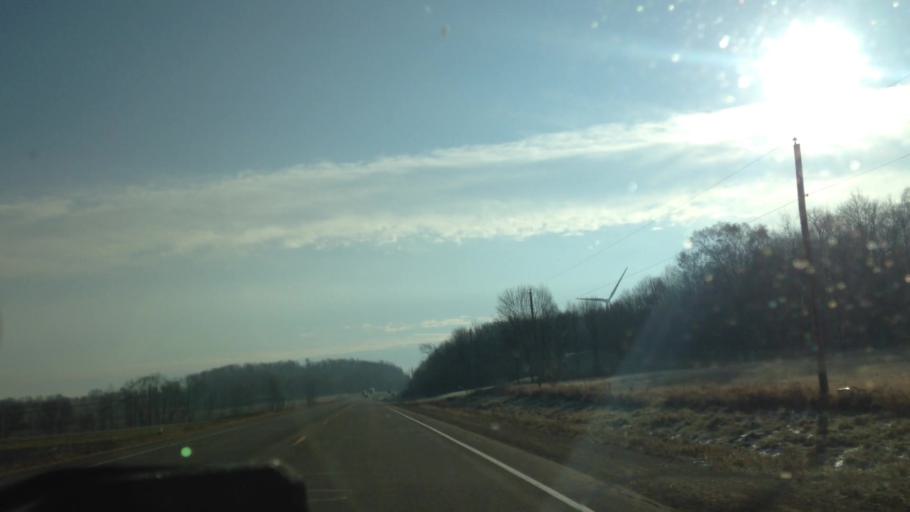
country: US
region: Wisconsin
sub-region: Dodge County
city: Mayville
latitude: 43.4412
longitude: -88.4867
